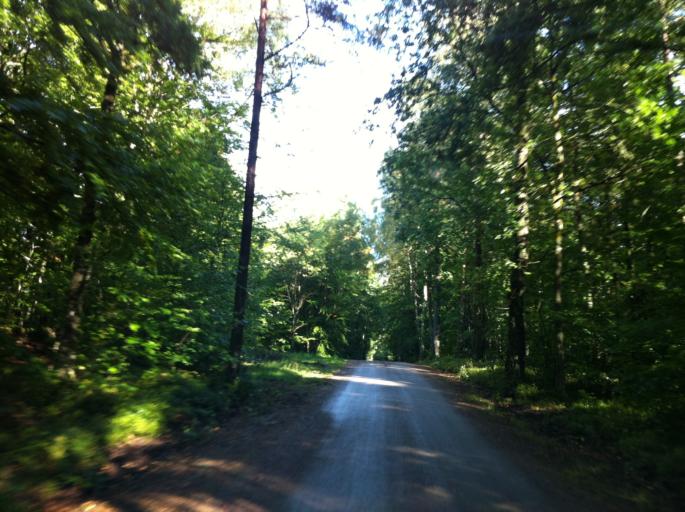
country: SE
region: Skane
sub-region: Hassleholms Kommun
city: Sosdala
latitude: 56.1338
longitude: 13.5541
